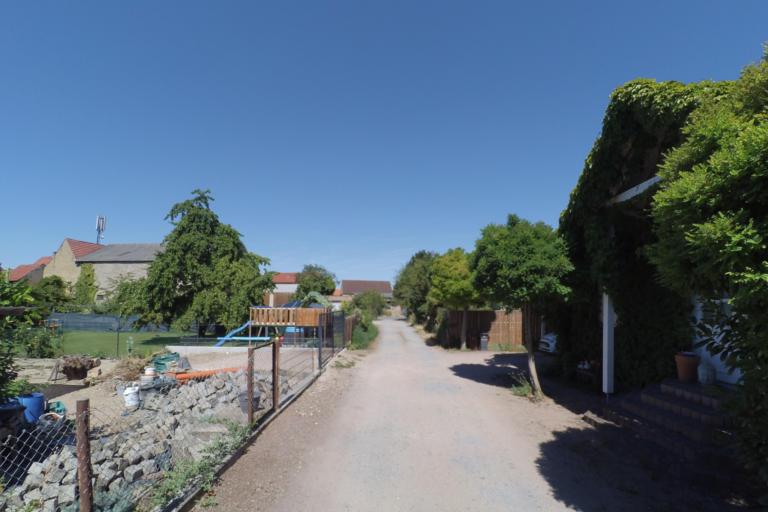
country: DE
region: Rheinland-Pfalz
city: Worms
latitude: 49.6800
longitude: 8.3882
